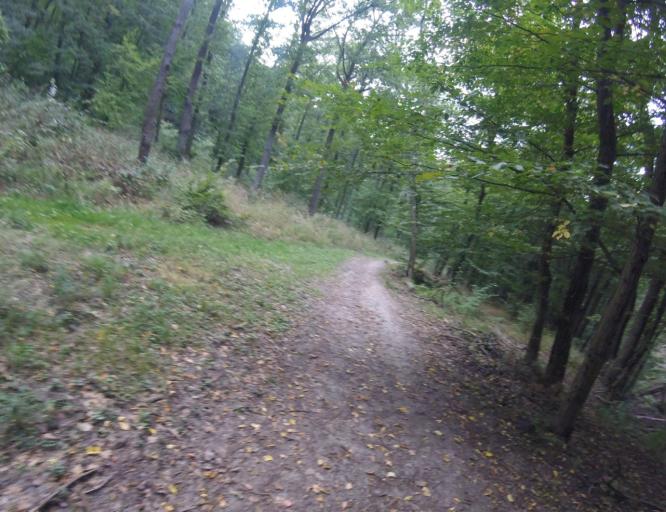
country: HU
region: Pest
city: Nagykovacsi
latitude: 47.6807
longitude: 19.0122
